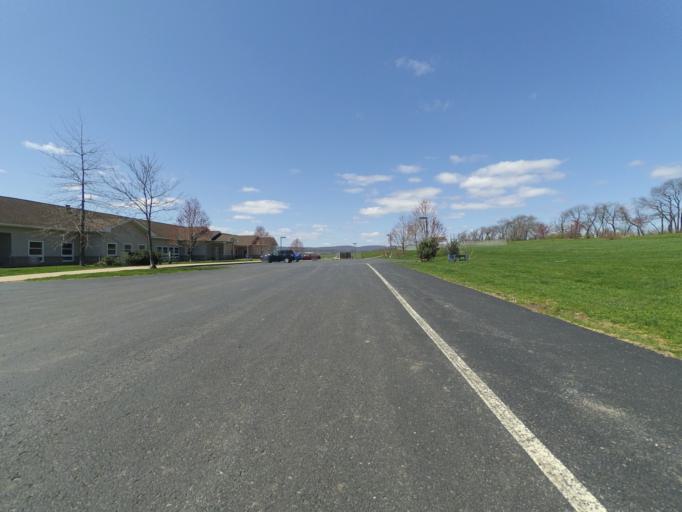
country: US
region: Pennsylvania
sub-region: Centre County
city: Houserville
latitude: 40.8364
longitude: -77.8110
